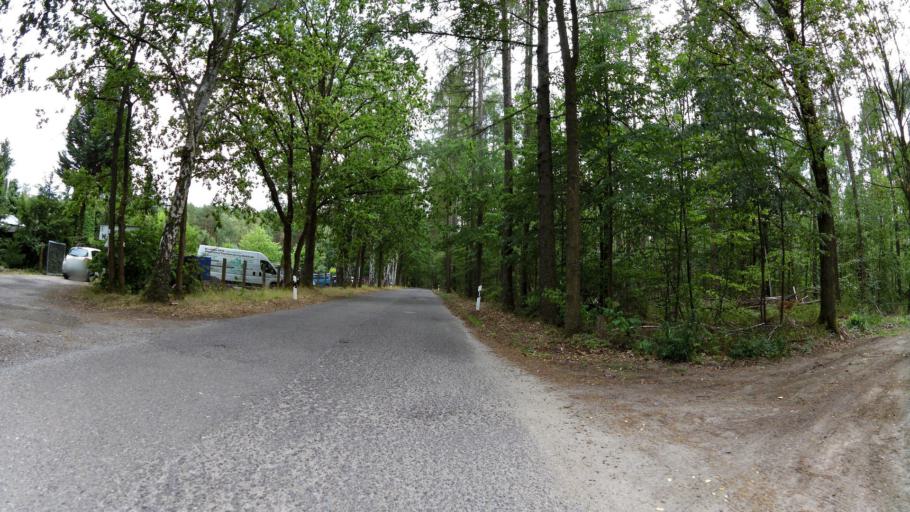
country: DE
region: Brandenburg
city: Spremberg
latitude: 51.6516
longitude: 14.3696
